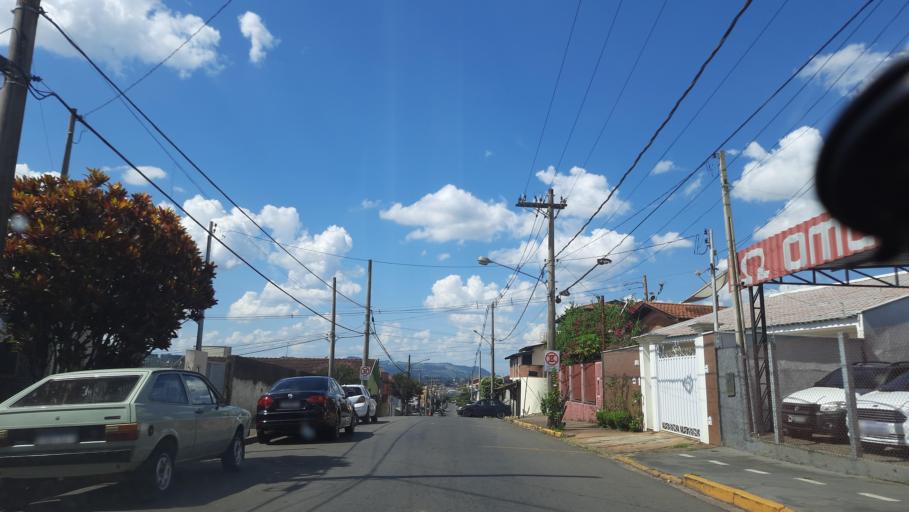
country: BR
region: Sao Paulo
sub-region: Sao Jose Do Rio Pardo
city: Sao Jose do Rio Pardo
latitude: -21.6035
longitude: -46.8977
